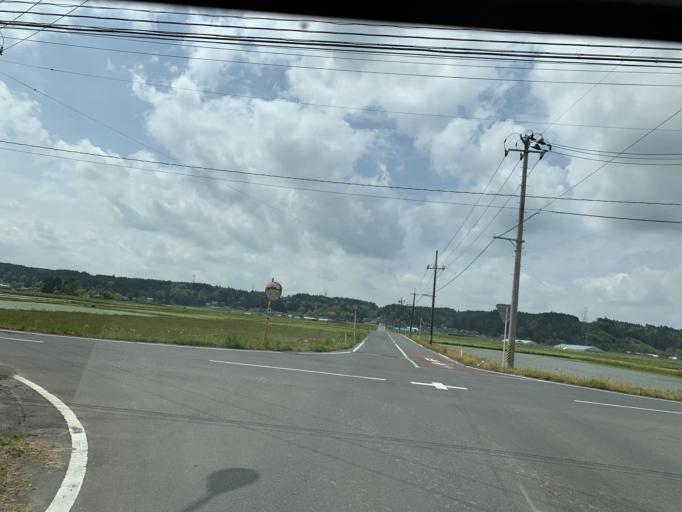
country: JP
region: Miyagi
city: Furukawa
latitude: 38.7479
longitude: 140.9343
